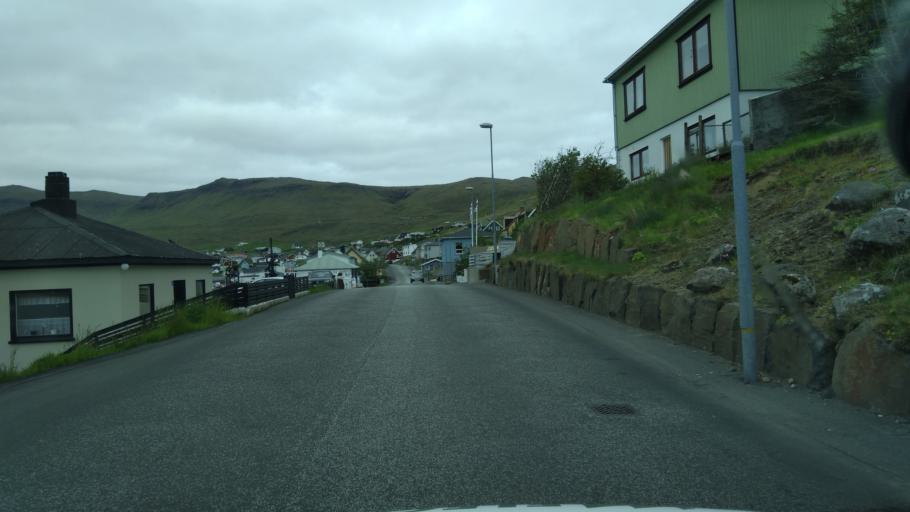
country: FO
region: Suduroy
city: Tvoroyri
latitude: 61.5593
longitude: -6.8232
